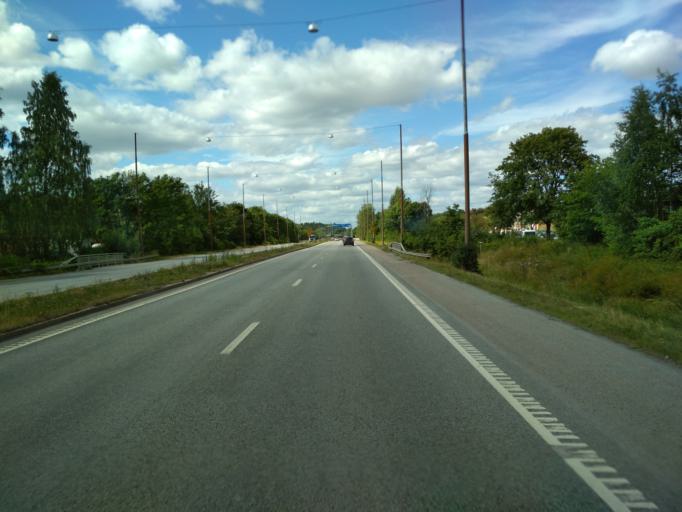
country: SE
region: Uppsala
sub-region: Uppsala Kommun
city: Uppsala
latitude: 59.8734
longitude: 17.6485
